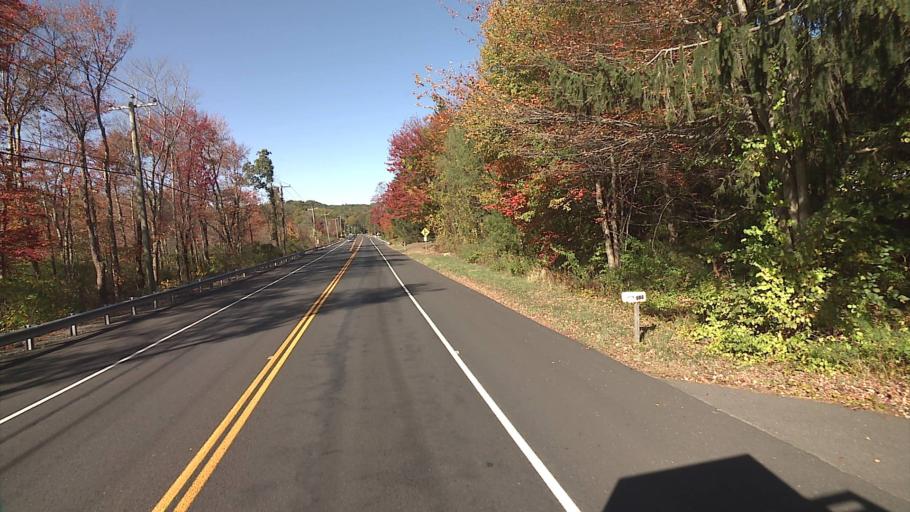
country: US
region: Connecticut
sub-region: Tolland County
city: Rockville
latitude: 41.7833
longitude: -72.4288
